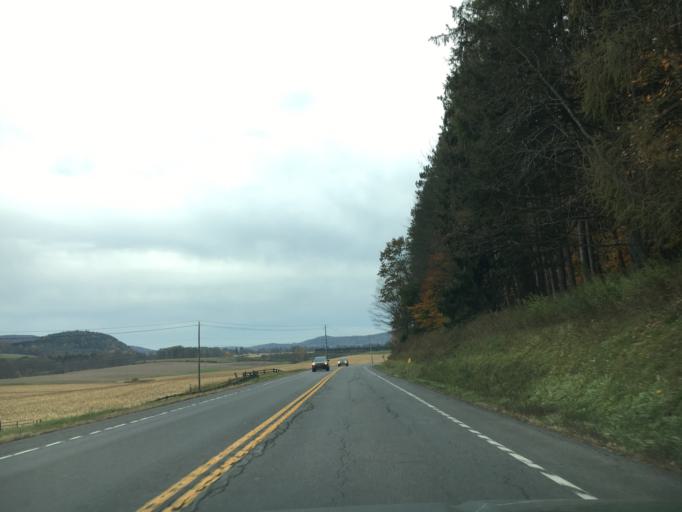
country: US
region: New York
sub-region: Otsego County
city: Cooperstown
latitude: 42.6831
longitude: -74.9444
